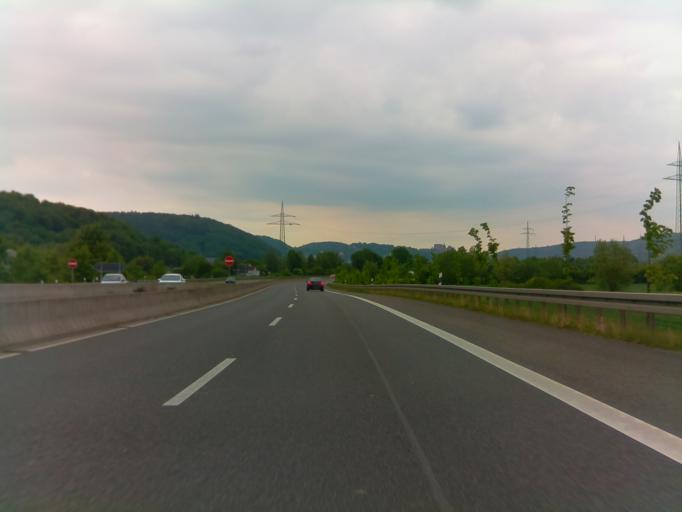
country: DE
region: Hesse
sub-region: Regierungsbezirk Giessen
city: Marburg an der Lahn
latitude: 50.7612
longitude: 8.7461
